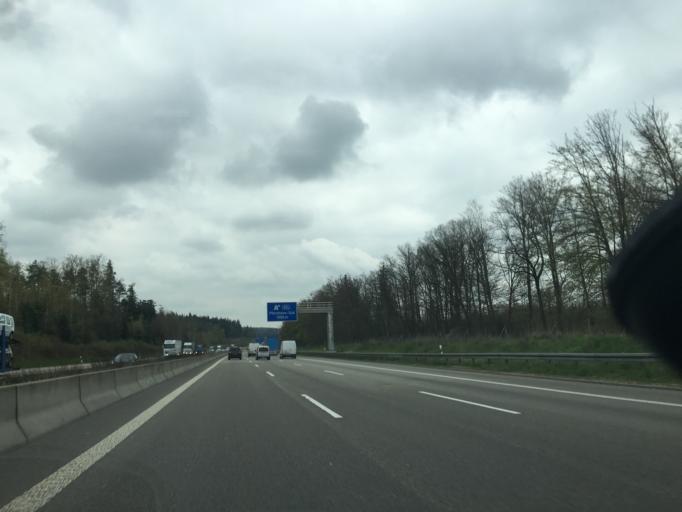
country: DE
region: Baden-Wuerttemberg
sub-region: Karlsruhe Region
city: Wurmberg
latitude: 48.8677
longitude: 8.7914
